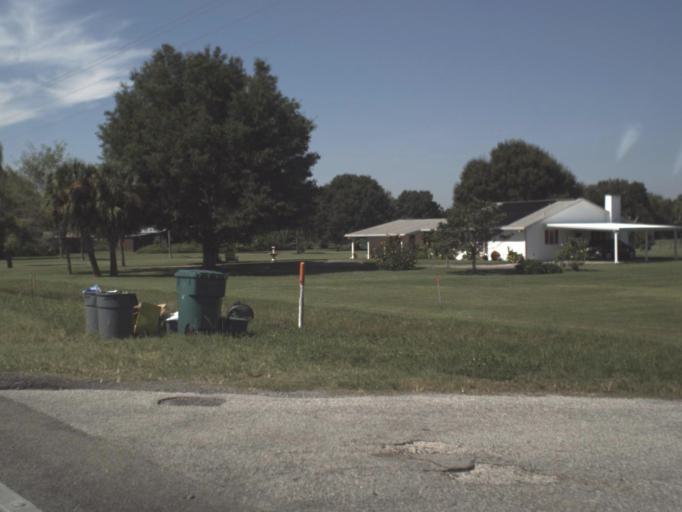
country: US
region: Florida
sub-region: Hendry County
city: Harlem
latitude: 26.7544
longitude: -80.9922
